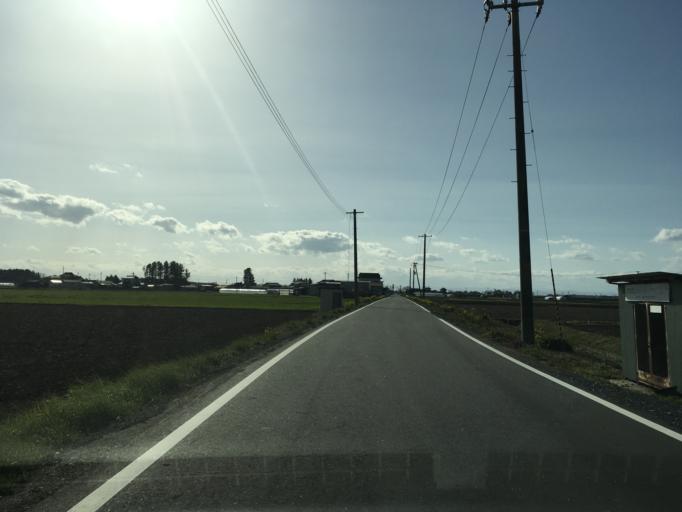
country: JP
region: Miyagi
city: Wakuya
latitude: 38.6598
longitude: 141.2240
